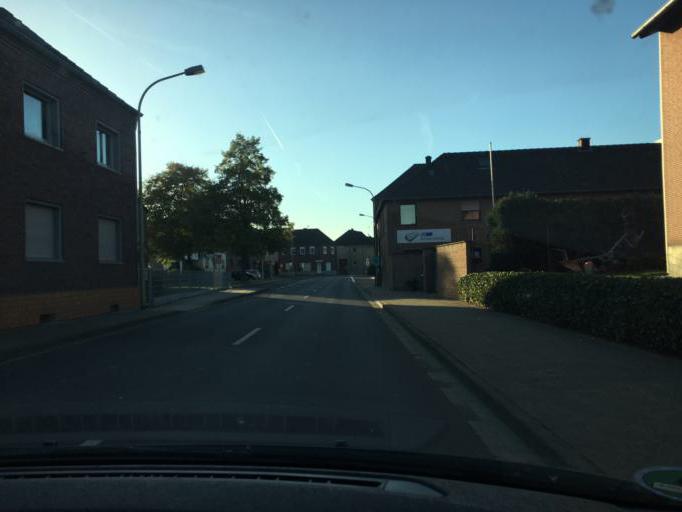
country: DE
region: North Rhine-Westphalia
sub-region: Regierungsbezirk Koln
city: Langerwehe
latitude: 50.8179
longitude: 6.4008
